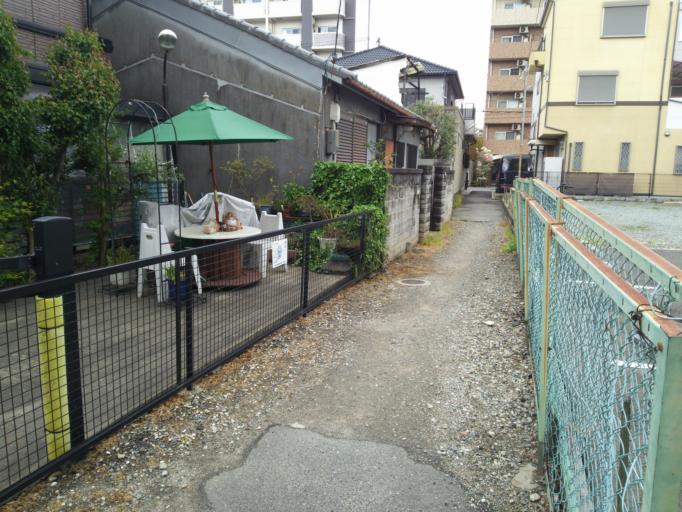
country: JP
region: Hyogo
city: Amagasaki
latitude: 34.7203
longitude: 135.4073
